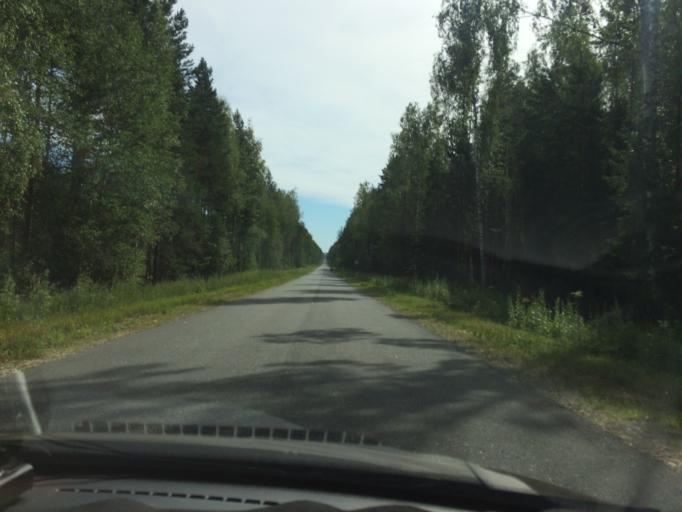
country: RU
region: Mariy-El
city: Mochalishche
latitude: 56.5487
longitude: 48.3313
